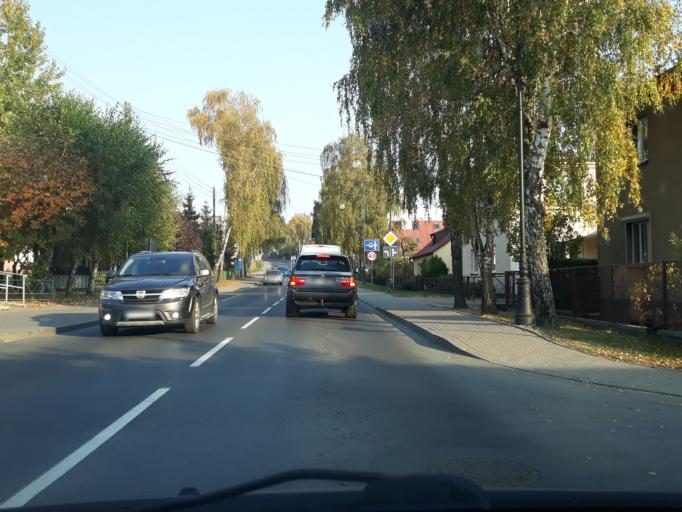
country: PL
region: Pomeranian Voivodeship
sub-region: Powiat chojnicki
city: Chojnice
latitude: 53.6885
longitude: 17.5646
